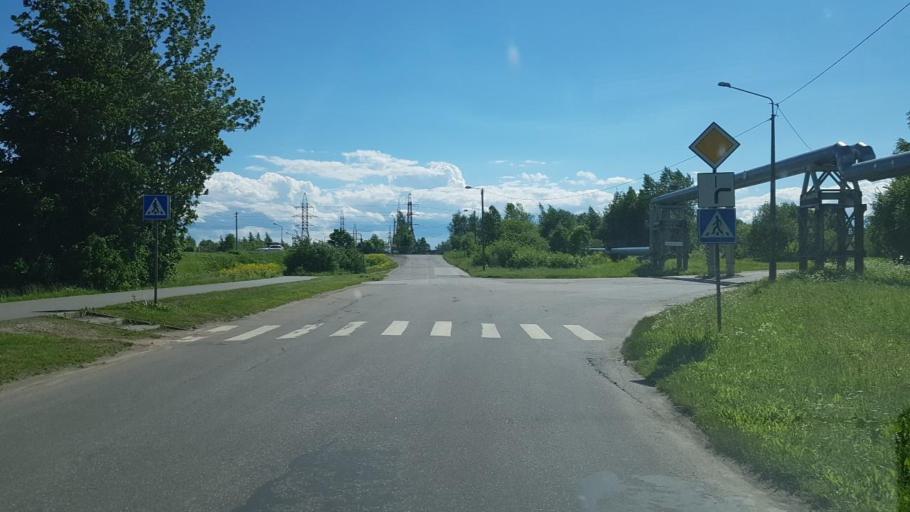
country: EE
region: Ida-Virumaa
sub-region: Narva linn
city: Narva
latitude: 59.3538
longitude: 28.1812
